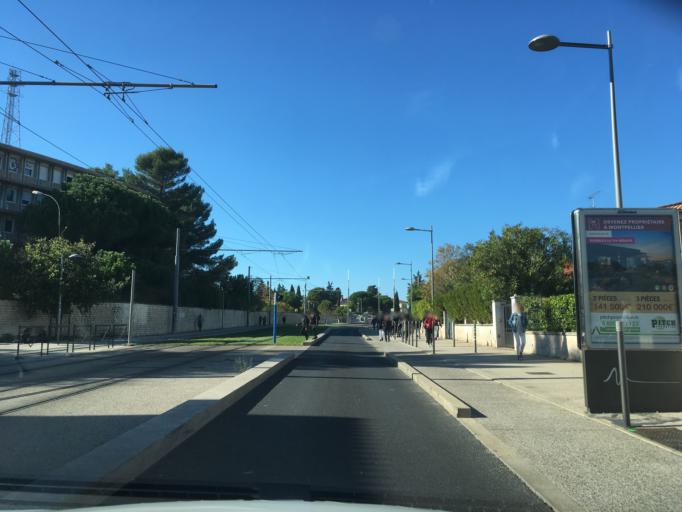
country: FR
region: Languedoc-Roussillon
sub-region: Departement de l'Herault
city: Montpellier
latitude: 43.6109
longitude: 3.8485
